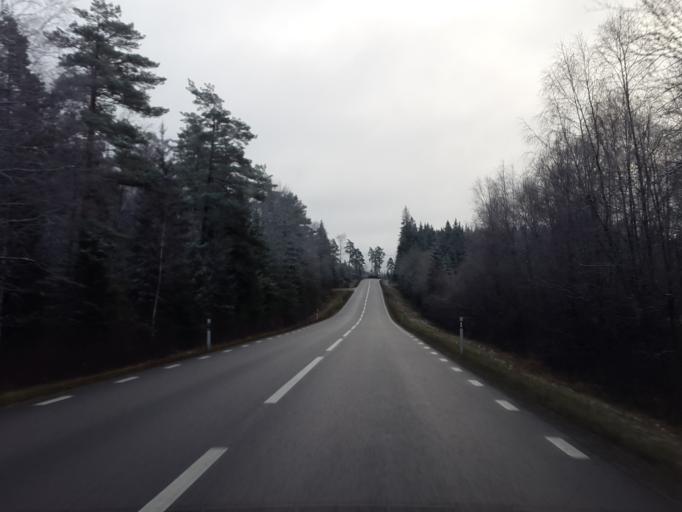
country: SE
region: Vaestra Goetaland
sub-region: Vargarda Kommun
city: Jonstorp
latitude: 57.8409
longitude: 12.6809
